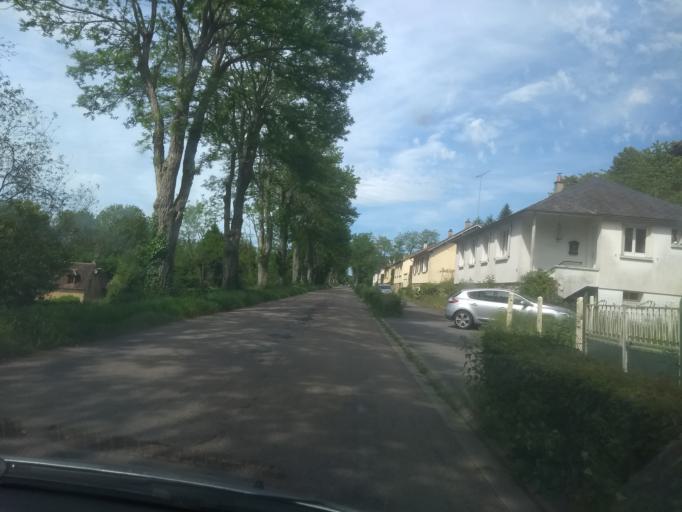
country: FR
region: Lower Normandy
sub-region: Departement de l'Orne
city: Longny-au-Perche
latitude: 48.5226
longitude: 0.7502
